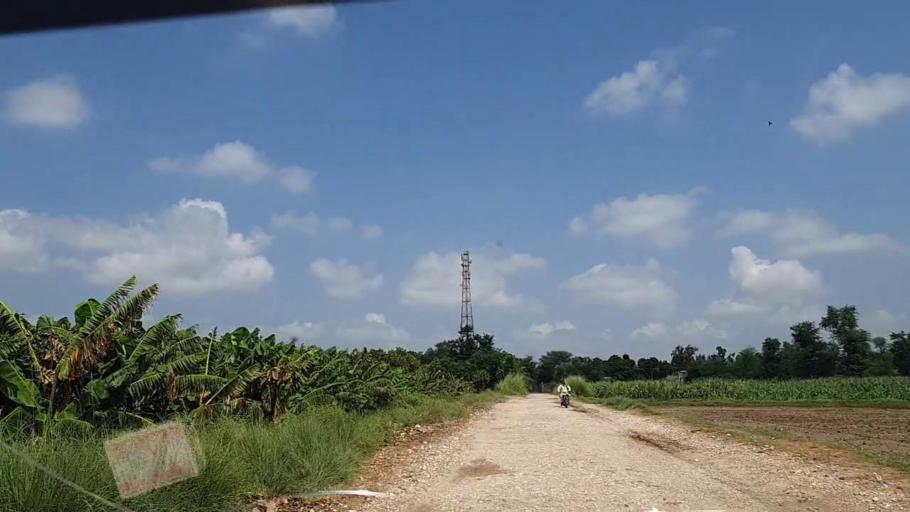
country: PK
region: Sindh
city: Tharu Shah
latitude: 26.9090
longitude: 68.0360
